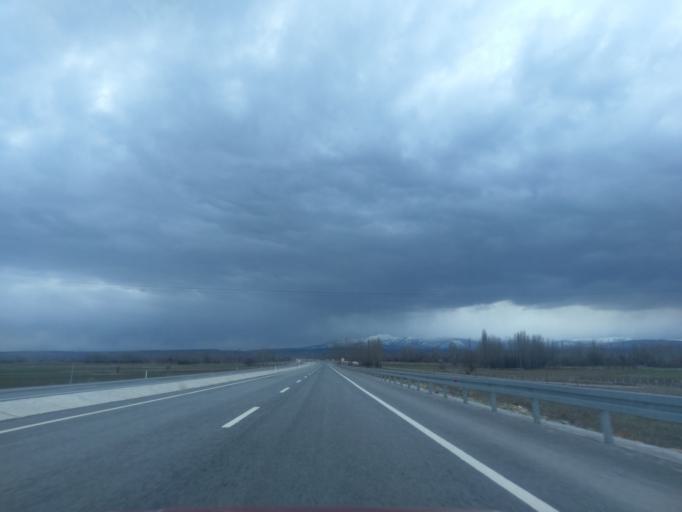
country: TR
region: Kuetahya
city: Cavdarhisar
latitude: 39.2152
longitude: 29.6606
